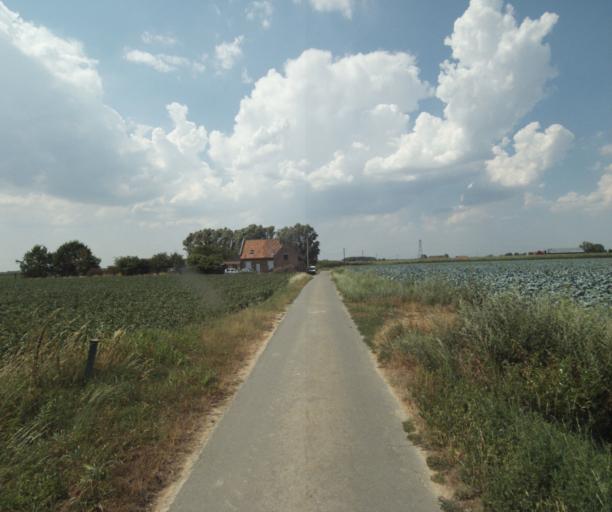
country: FR
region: Nord-Pas-de-Calais
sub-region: Departement du Nord
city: Quesnoy-sur-Deule
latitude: 50.7372
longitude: 2.9959
